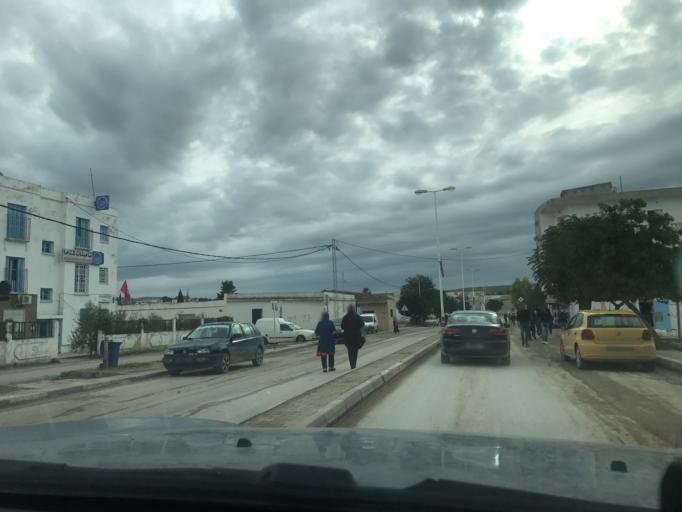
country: TN
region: Silyanah
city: Siliana
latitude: 36.0927
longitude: 9.5682
